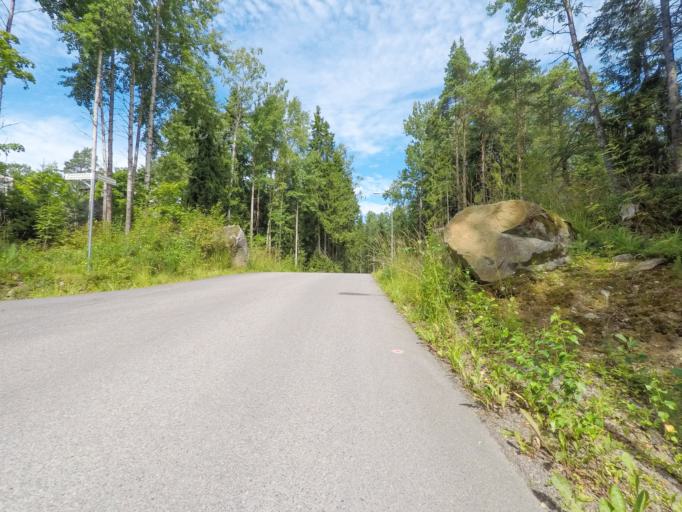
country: FI
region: Uusimaa
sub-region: Helsinki
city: Vantaa
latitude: 60.1652
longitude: 25.0900
